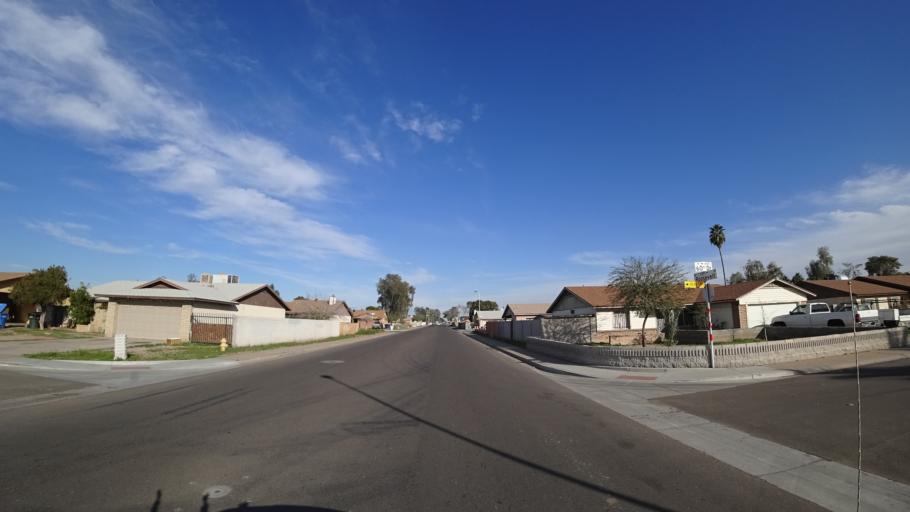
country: US
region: Arizona
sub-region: Maricopa County
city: Tolleson
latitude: 33.4588
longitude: -112.1895
